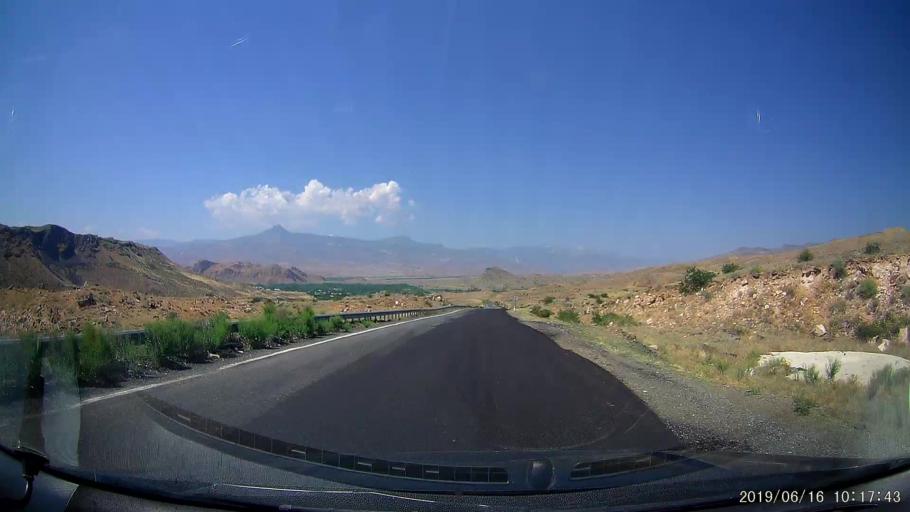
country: TR
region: Igdir
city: Tuzluca
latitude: 40.1670
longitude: 43.6817
